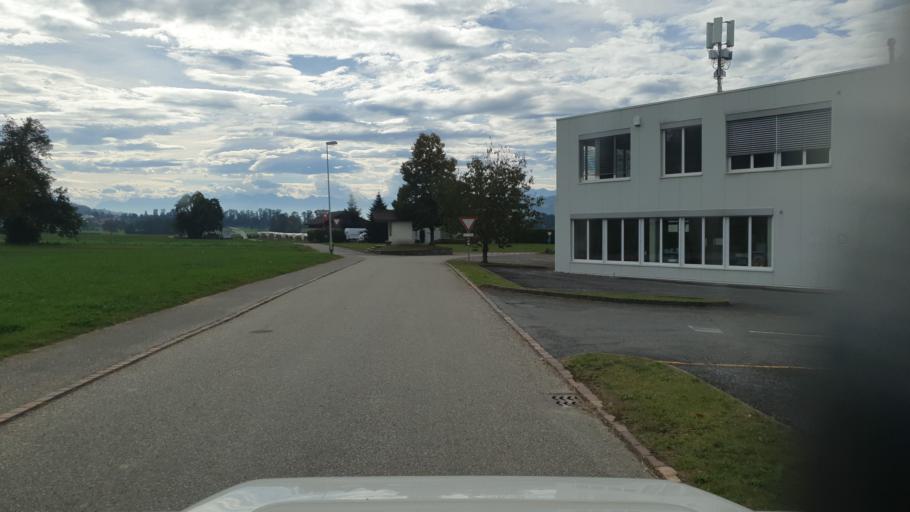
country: CH
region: Lucerne
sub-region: Hochdorf District
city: Hitzkirch
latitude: 47.2524
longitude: 8.2385
